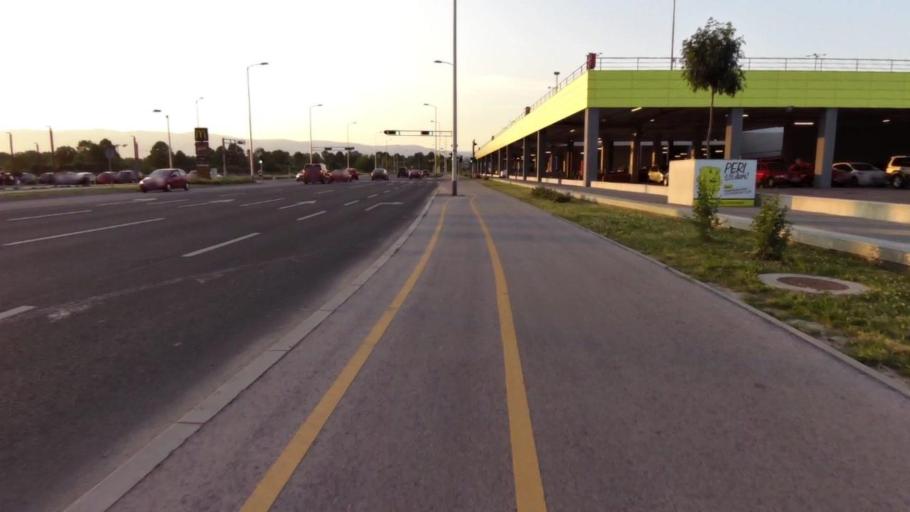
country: HR
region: Grad Zagreb
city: Dubrava
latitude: 45.8015
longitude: 16.0489
